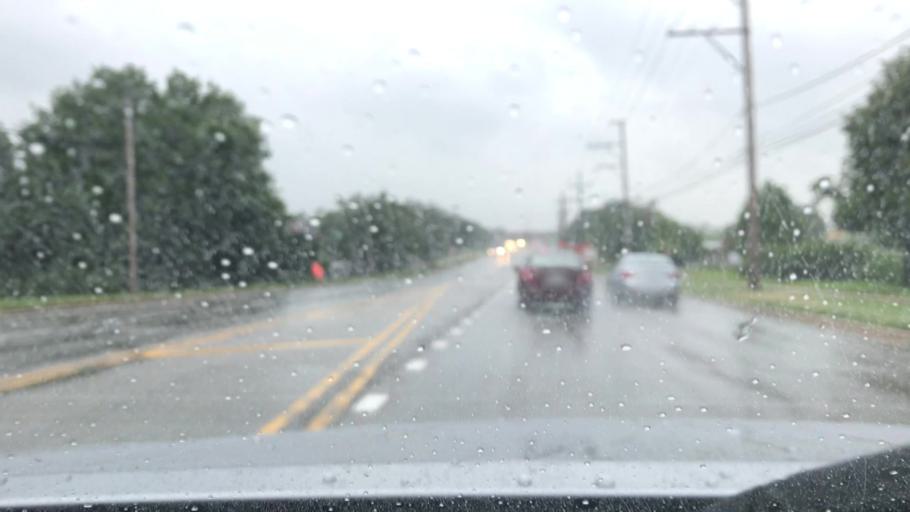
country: US
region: Illinois
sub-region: DuPage County
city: Lisle
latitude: 41.8049
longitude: -88.0476
